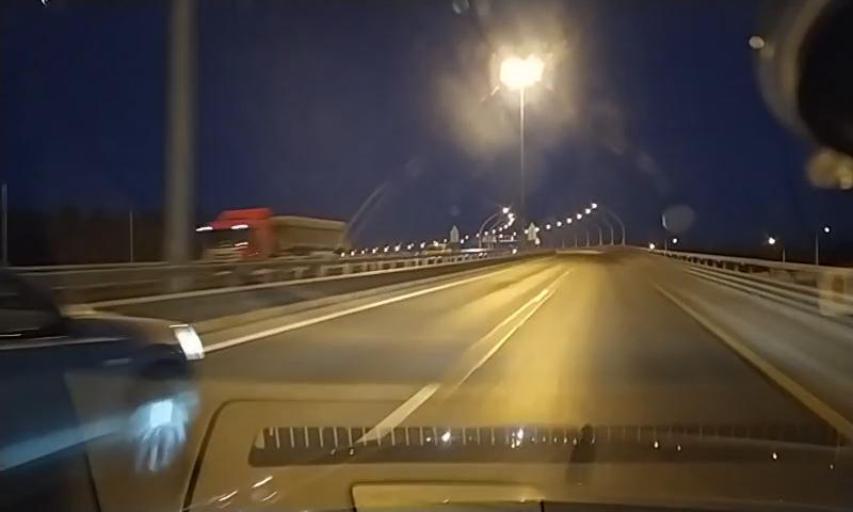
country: RU
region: St.-Petersburg
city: Beloostrov
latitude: 60.1335
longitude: 30.0606
